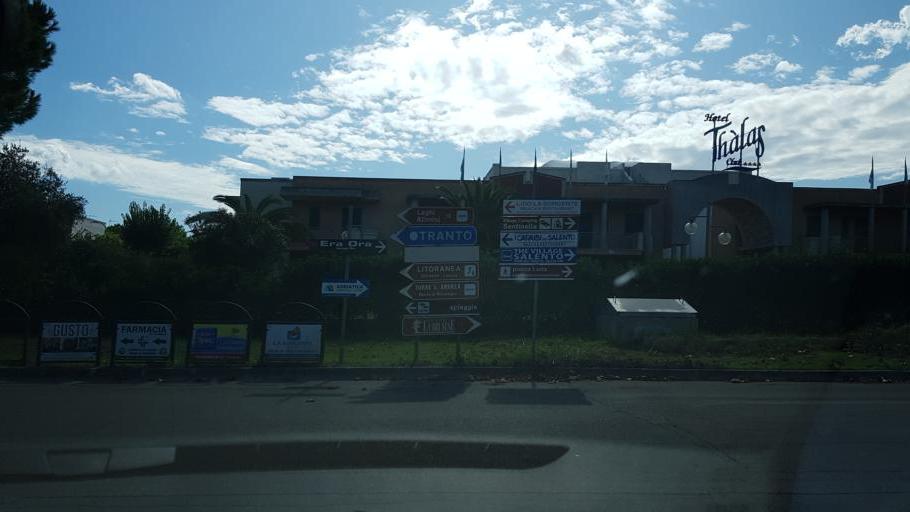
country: IT
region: Apulia
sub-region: Provincia di Lecce
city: Borgagne
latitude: 40.2722
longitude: 18.4237
